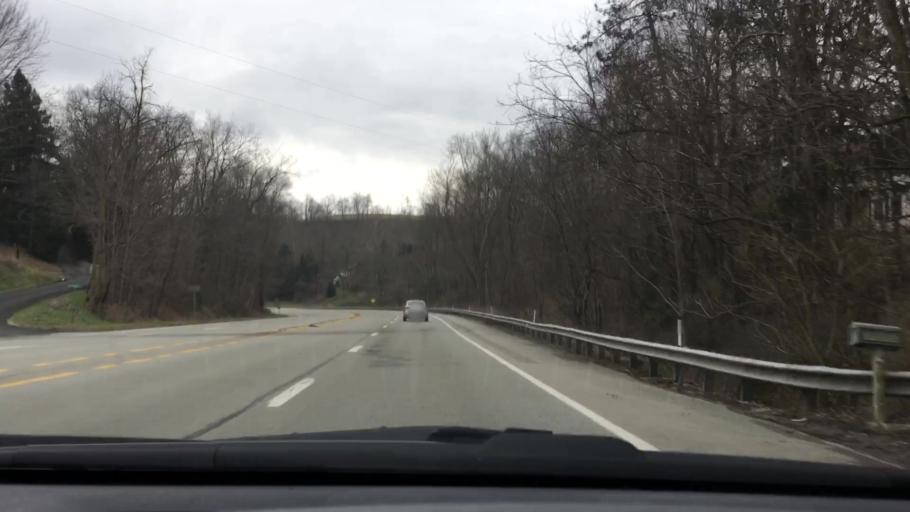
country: US
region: Pennsylvania
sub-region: Fayette County
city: Perryopolis
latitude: 40.0151
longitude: -79.7661
